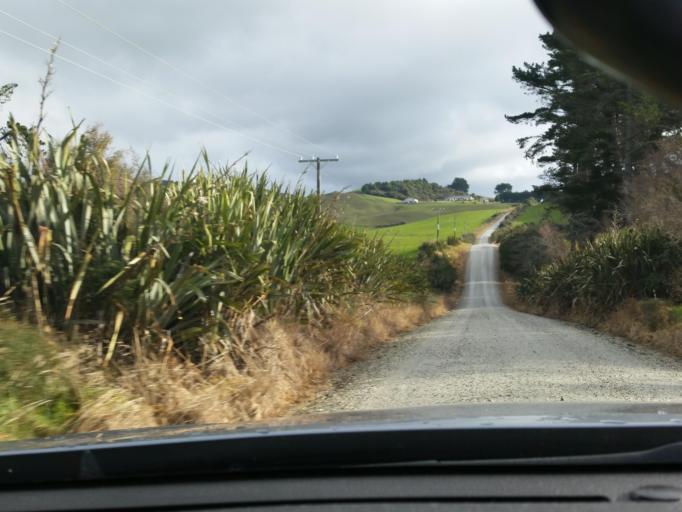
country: NZ
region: Southland
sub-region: Gore District
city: Gore
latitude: -46.5380
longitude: 168.9865
